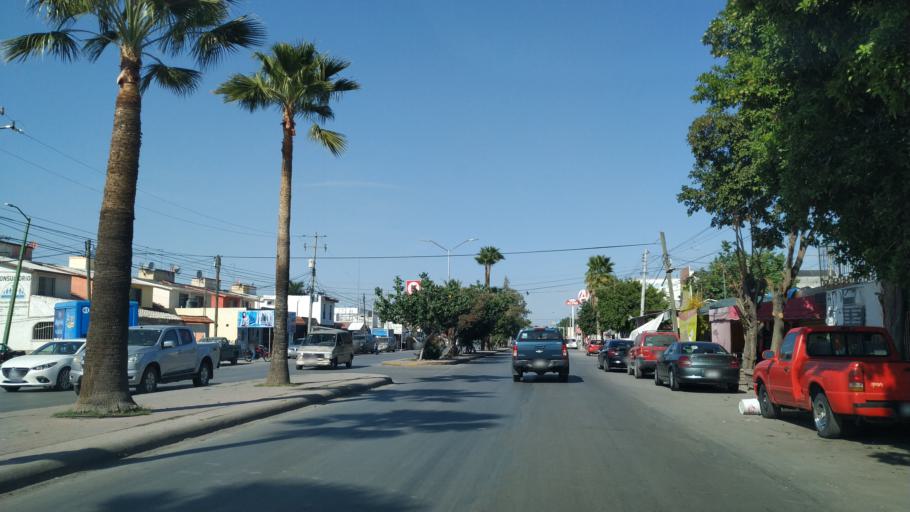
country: MX
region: Coahuila
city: Torreon
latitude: 25.5360
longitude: -103.3959
